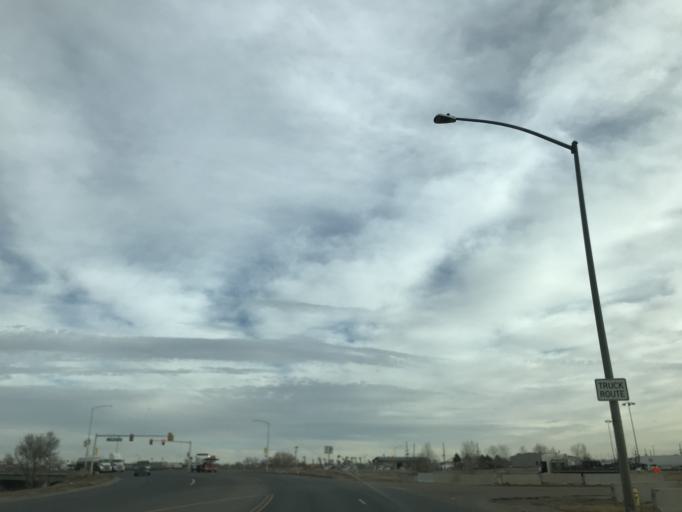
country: US
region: Colorado
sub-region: Adams County
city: Commerce City
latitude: 39.7966
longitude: -104.9349
